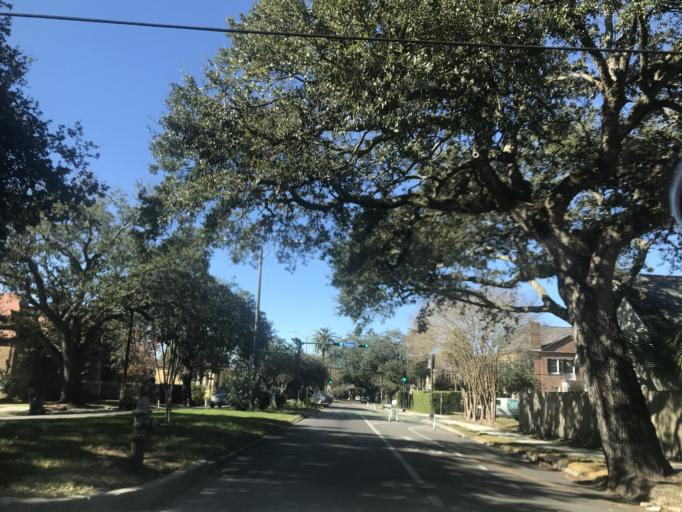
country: US
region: Louisiana
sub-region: Orleans Parish
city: New Orleans
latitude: 29.9509
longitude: -90.1081
